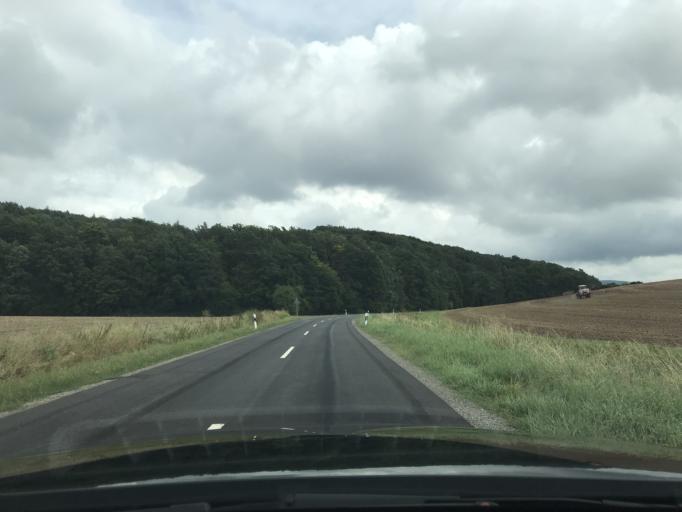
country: DE
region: Bavaria
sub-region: Regierungsbezirk Unterfranken
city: Kirchlauter
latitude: 50.0601
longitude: 10.6818
